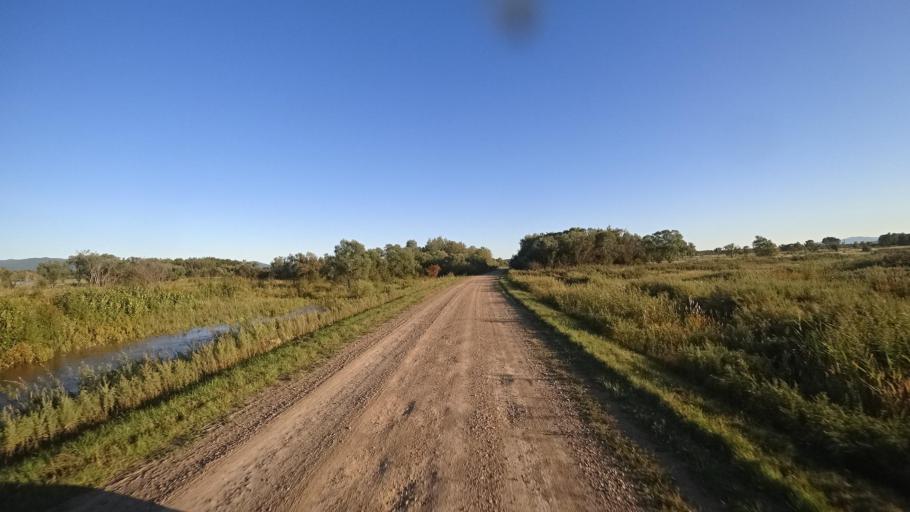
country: RU
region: Primorskiy
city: Kirovskiy
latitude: 44.7835
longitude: 133.6252
